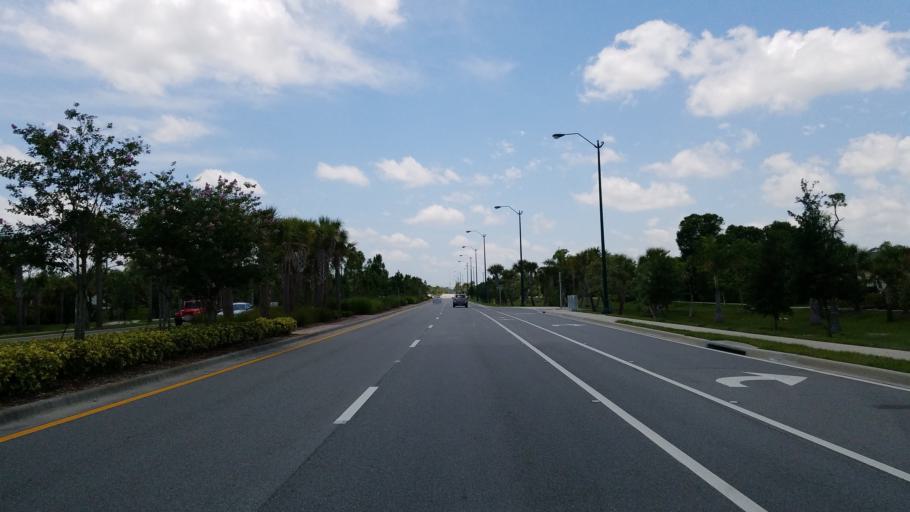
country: US
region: Florida
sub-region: Martin County
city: Palm City
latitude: 27.1613
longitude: -80.2610
